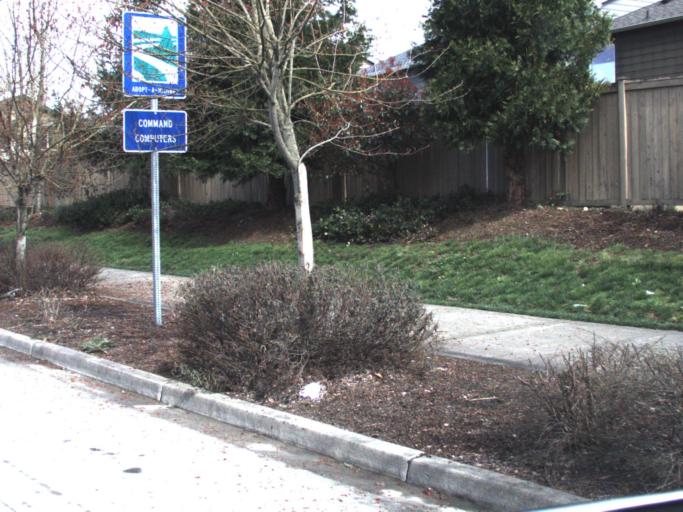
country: US
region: Washington
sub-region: King County
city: Maple Valley
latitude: 47.3668
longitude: -122.0221
